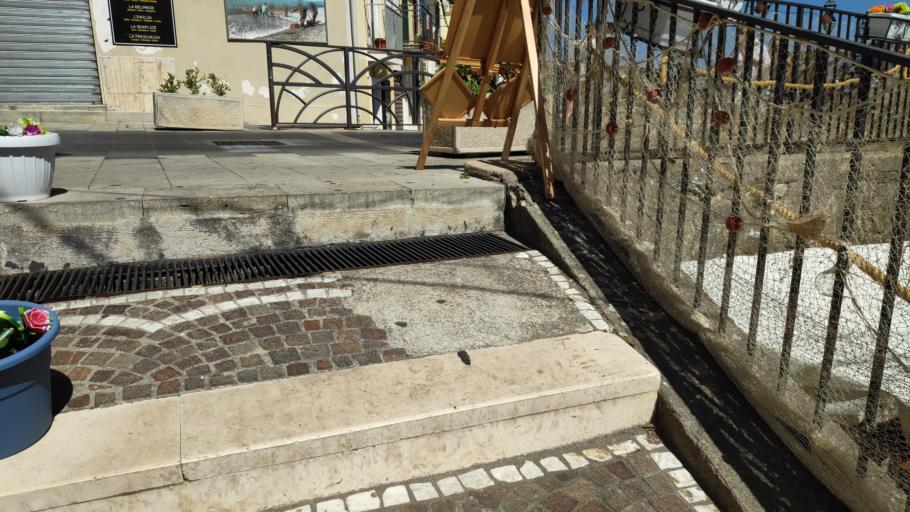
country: IT
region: Calabria
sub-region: Provincia di Cosenza
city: Diamante
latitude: 39.6781
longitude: 15.8184
